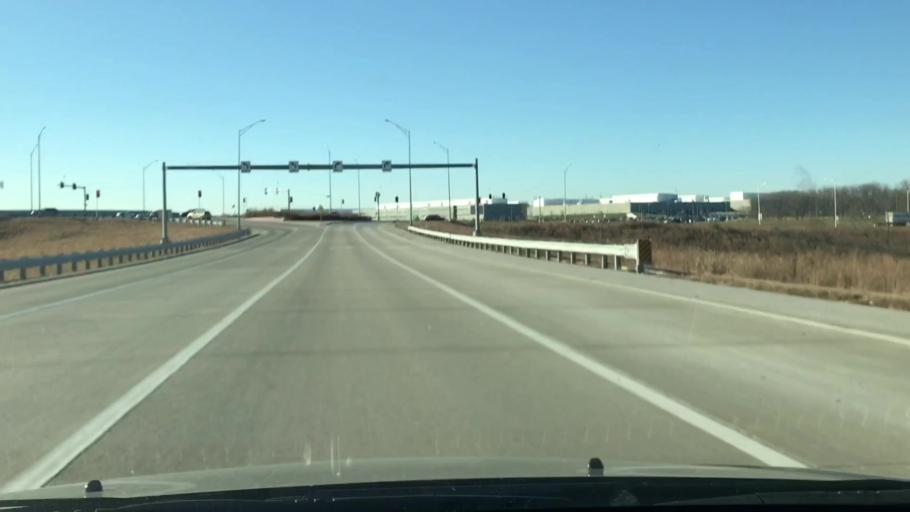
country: US
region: Missouri
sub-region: Jackson County
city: Grandview
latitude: 38.8591
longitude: -94.5447
